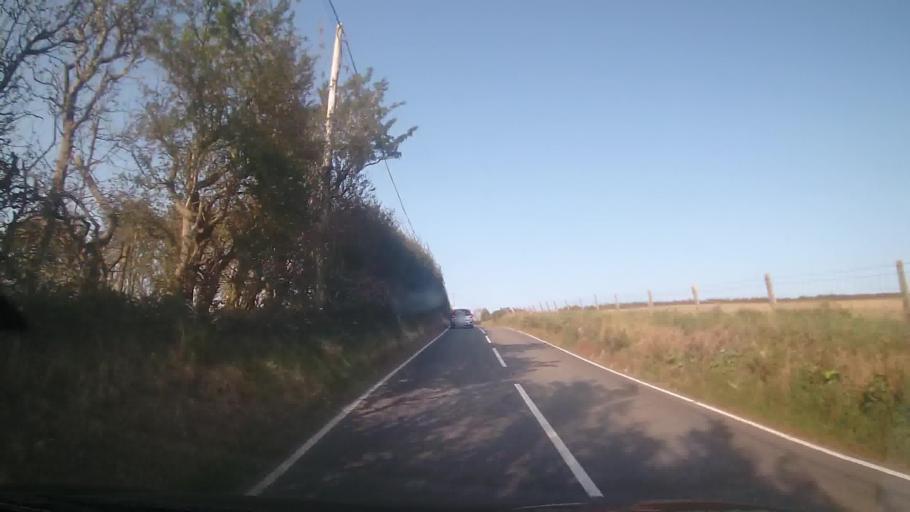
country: GB
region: Wales
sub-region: County of Ceredigion
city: Lledrod
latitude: 52.2915
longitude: -3.8611
